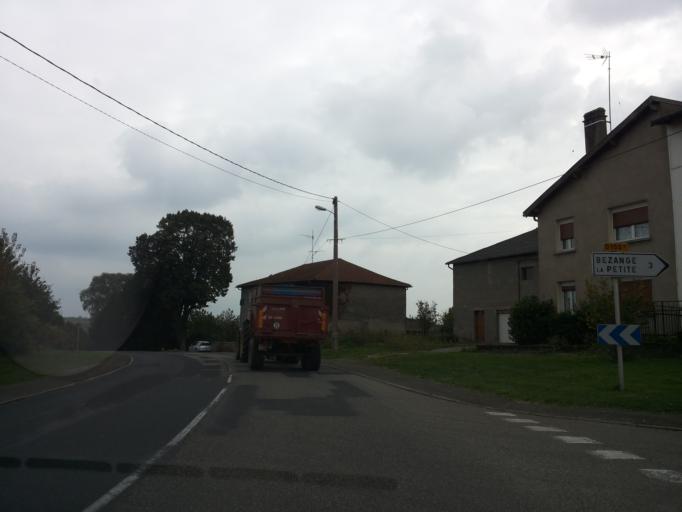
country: FR
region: Lorraine
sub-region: Departement de la Moselle
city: Vic-sur-Seille
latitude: 48.7517
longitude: 6.6295
